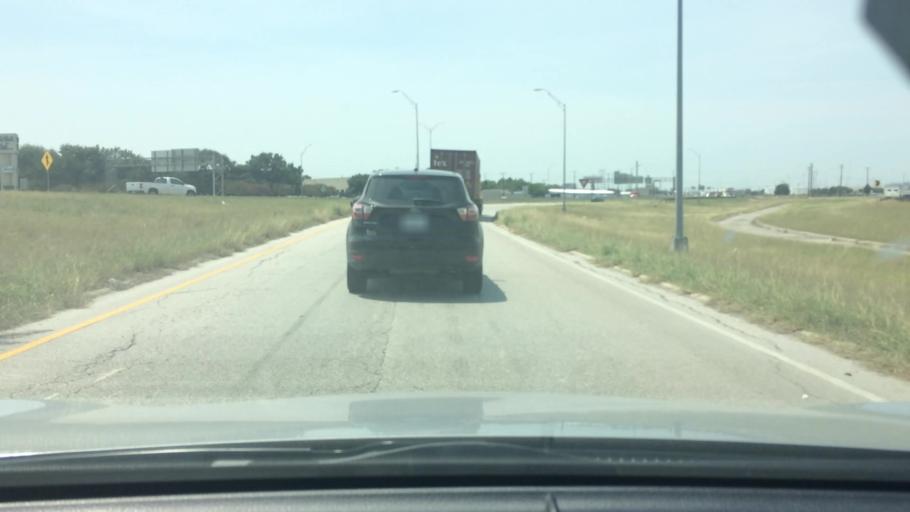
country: US
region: Texas
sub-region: Bexar County
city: Kirby
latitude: 29.4381
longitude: -98.3901
